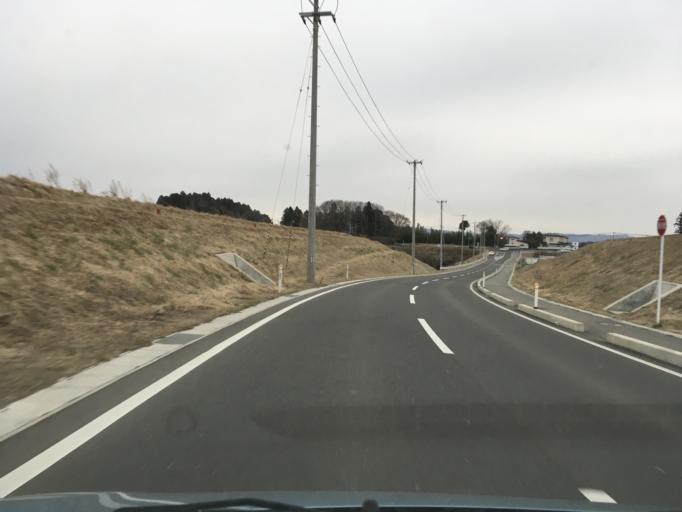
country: JP
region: Miyagi
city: Wakuya
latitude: 38.6950
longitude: 141.1711
